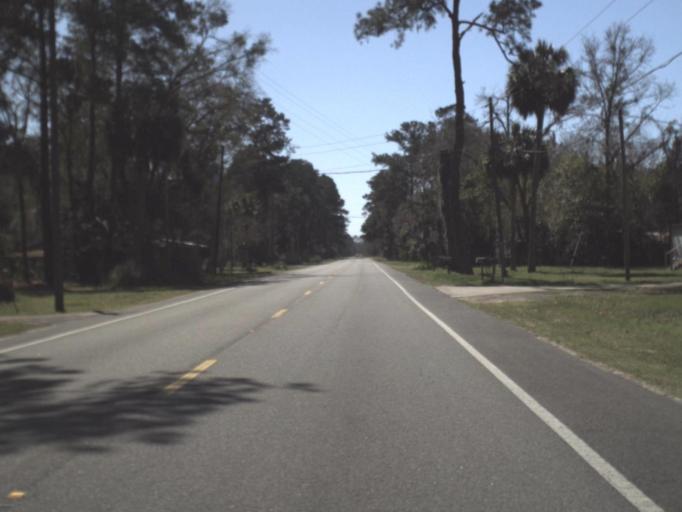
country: US
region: Florida
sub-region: Jefferson County
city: Monticello
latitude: 30.3553
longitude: -83.9902
